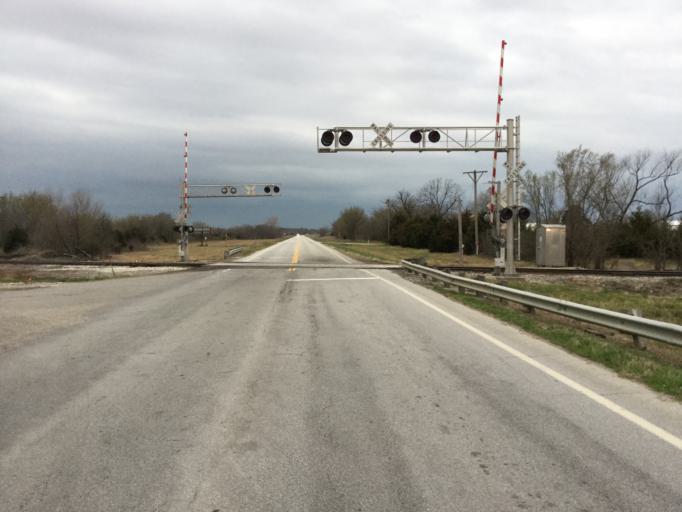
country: US
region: Kansas
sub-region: Cherokee County
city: Columbus
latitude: 37.1788
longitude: -94.9482
